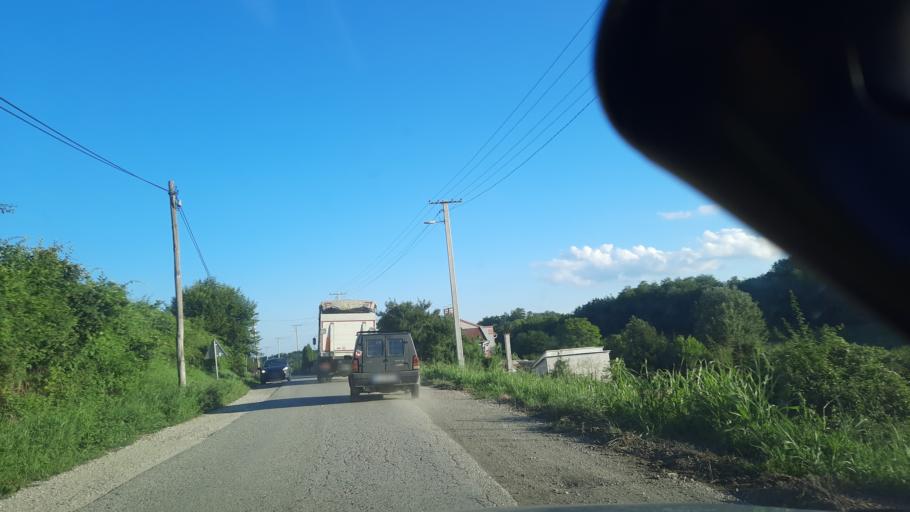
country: RS
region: Autonomna Pokrajina Vojvodina
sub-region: Juznobacki Okrug
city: Sremski Karlovci
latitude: 45.1217
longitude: 19.9438
